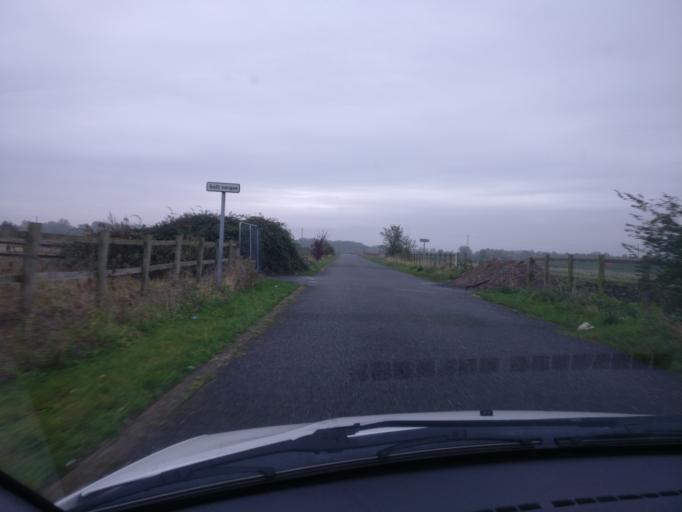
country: GB
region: England
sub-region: Peterborough
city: Eye
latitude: 52.5753
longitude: -0.1874
